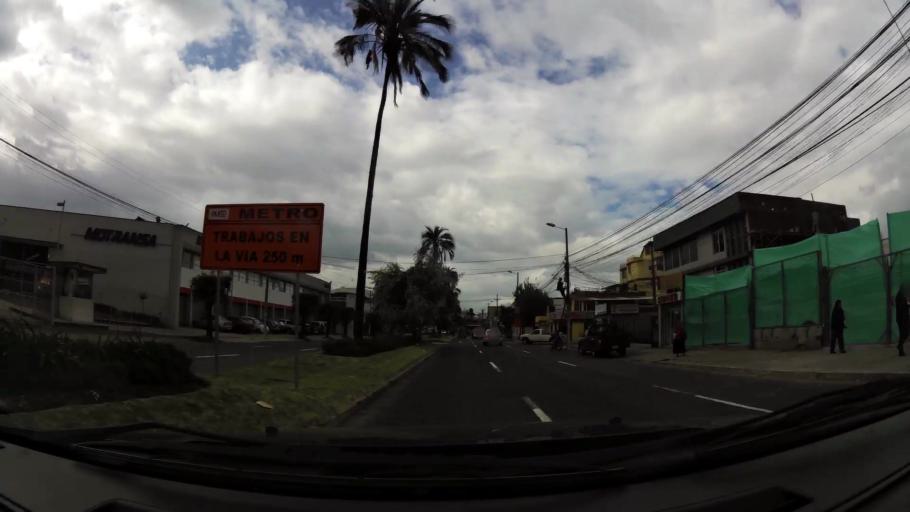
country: EC
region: Pichincha
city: Quito
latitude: -0.1660
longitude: -78.4854
